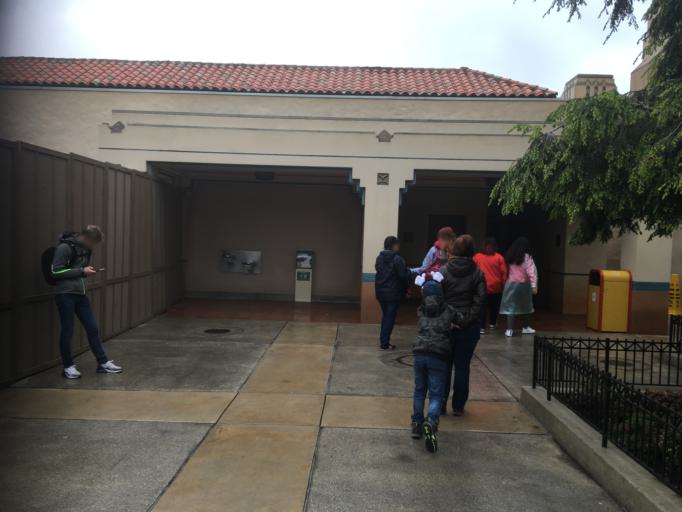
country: FR
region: Ile-de-France
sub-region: Departement de Seine-et-Marne
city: Chessy
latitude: 48.8665
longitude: 2.7791
